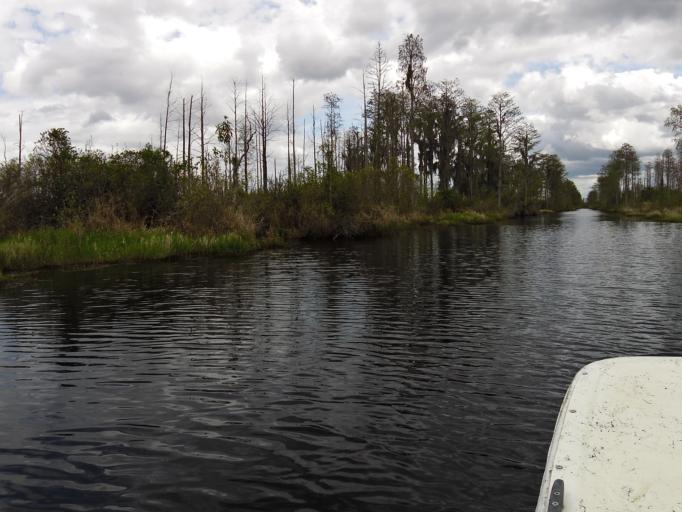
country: US
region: Georgia
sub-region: Charlton County
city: Folkston
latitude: 30.7363
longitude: -82.1644
